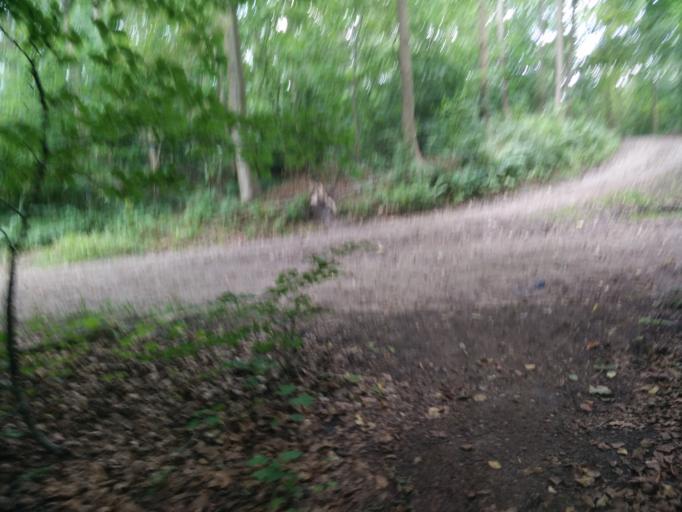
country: DK
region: Capital Region
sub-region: Frederikssund Kommune
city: Slangerup
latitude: 55.8597
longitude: 12.1991
